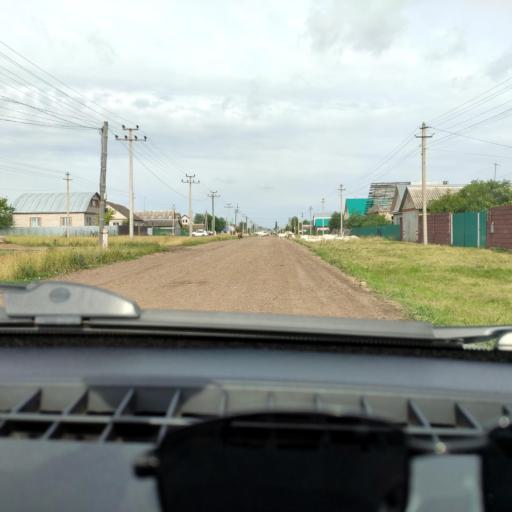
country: RU
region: Bashkortostan
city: Ulukulevo
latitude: 54.4209
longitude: 56.3372
